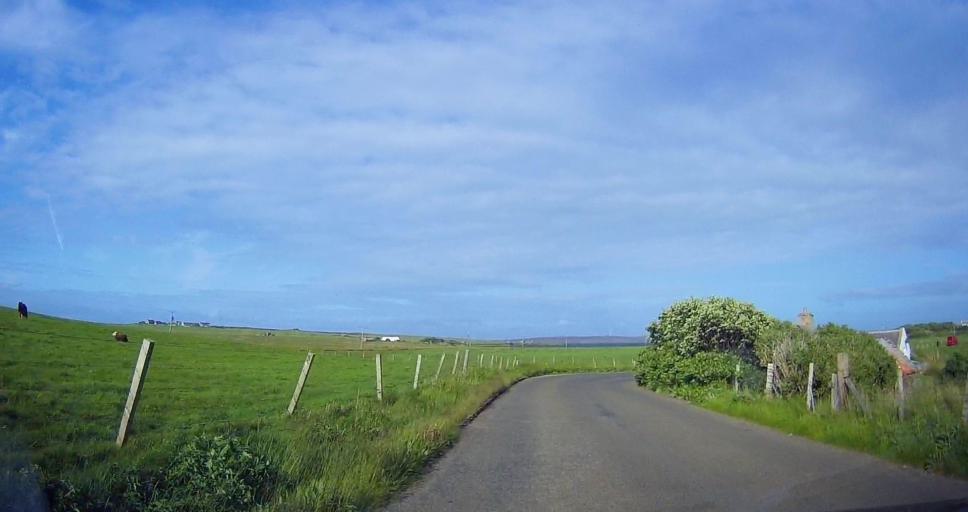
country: GB
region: Scotland
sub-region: Orkney Islands
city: Stromness
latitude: 58.8070
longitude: -3.2118
